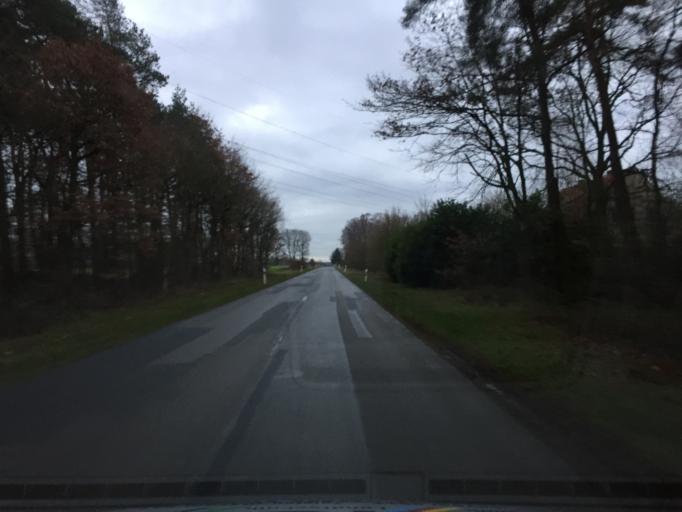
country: DE
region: Lower Saxony
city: Pennigsehl
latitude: 52.6429
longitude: 9.0024
